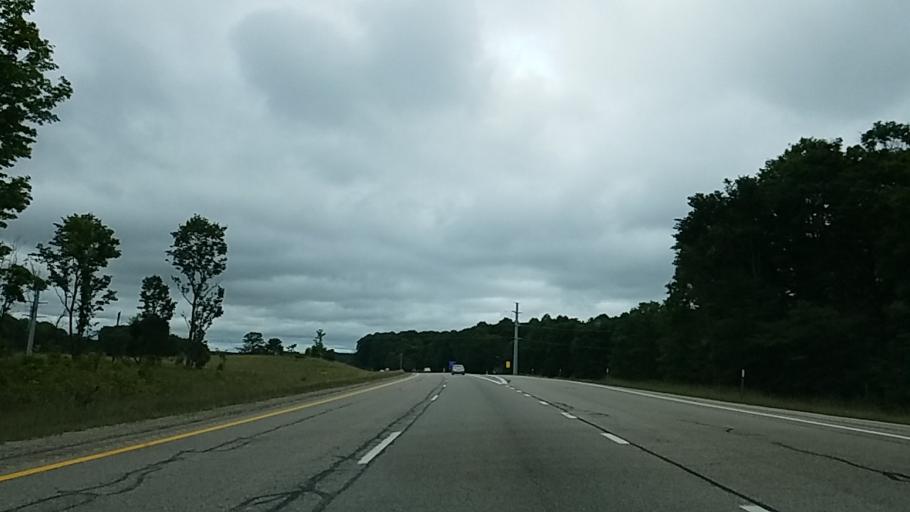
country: US
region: Michigan
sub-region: Otsego County
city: Gaylord
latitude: 45.1109
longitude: -84.6872
